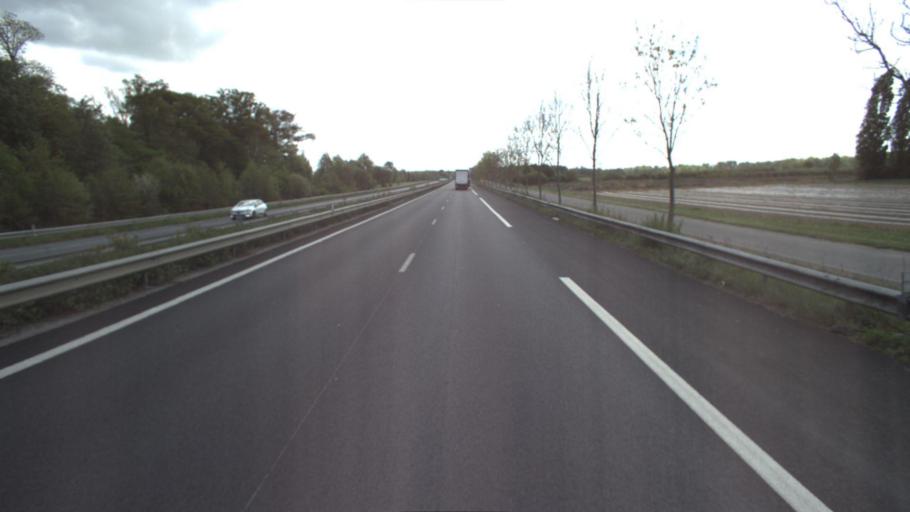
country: FR
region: Ile-de-France
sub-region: Departement de Seine-et-Marne
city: Fontenay-Tresigny
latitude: 48.7239
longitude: 2.8290
